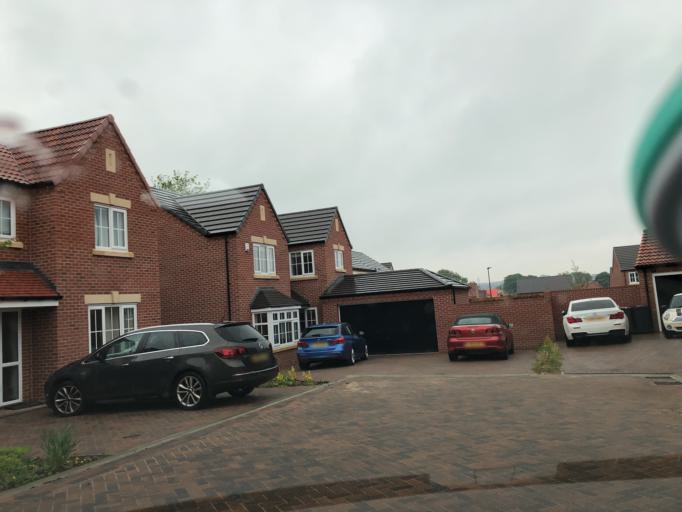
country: GB
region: England
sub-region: North Yorkshire
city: Harrogate
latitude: 54.0080
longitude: -1.5679
